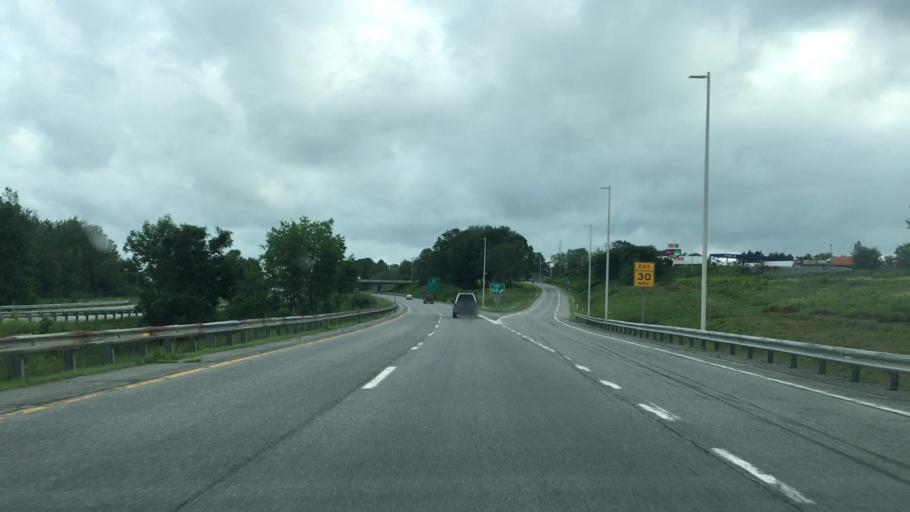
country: US
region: Maine
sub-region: Somerset County
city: Fairfield
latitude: 44.5972
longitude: -69.6129
